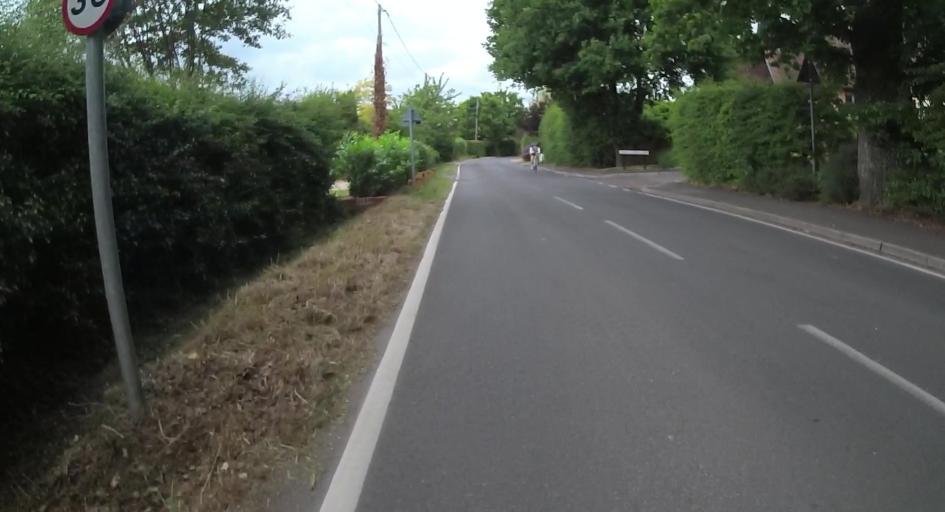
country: GB
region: England
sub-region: Hampshire
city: Fleet
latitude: 51.2791
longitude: -0.8865
